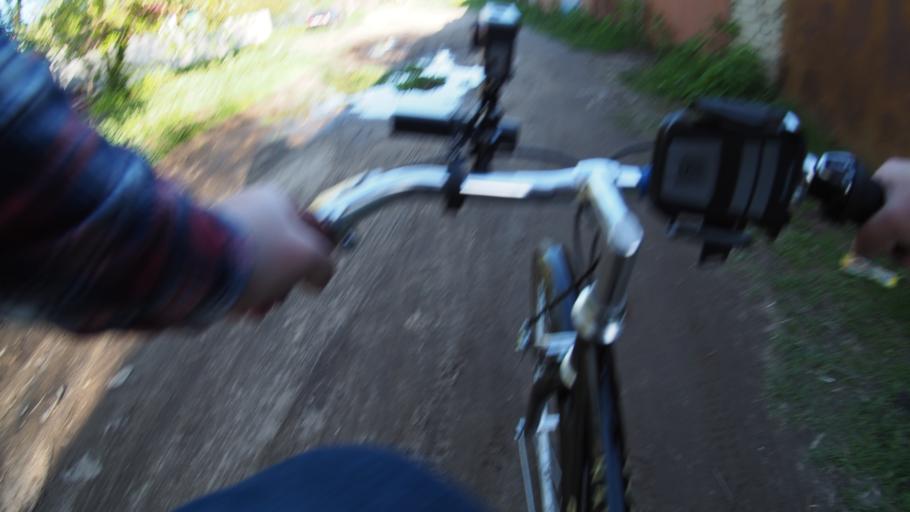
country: RU
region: Moskovskaya
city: Ramenskoye
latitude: 55.5592
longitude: 38.2088
